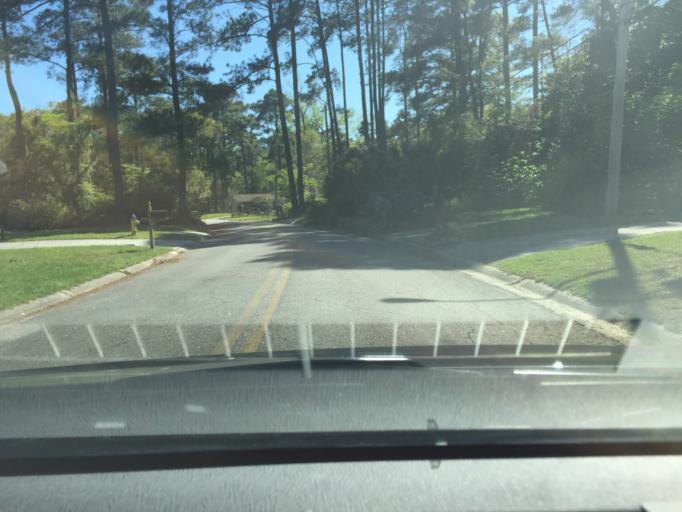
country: US
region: Georgia
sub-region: Chatham County
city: Montgomery
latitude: 31.9828
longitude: -81.1082
